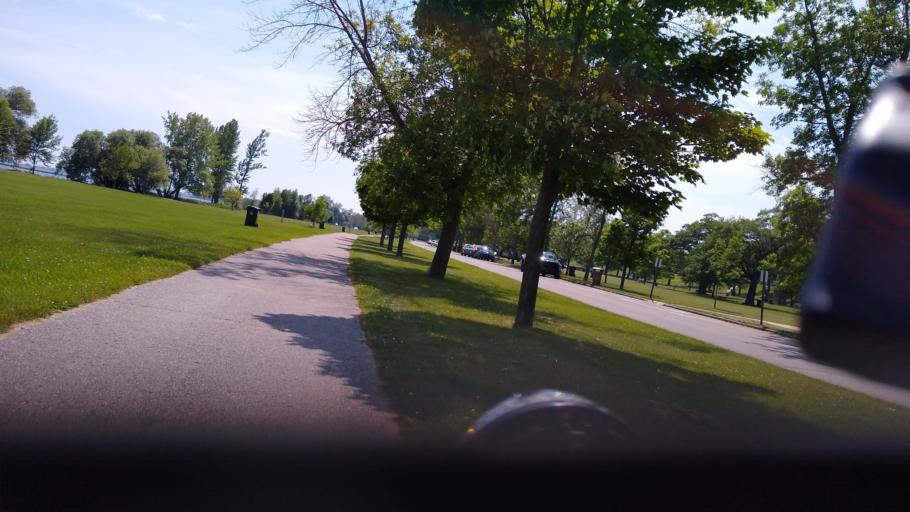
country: US
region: Michigan
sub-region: Delta County
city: Escanaba
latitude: 45.7411
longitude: -87.0507
